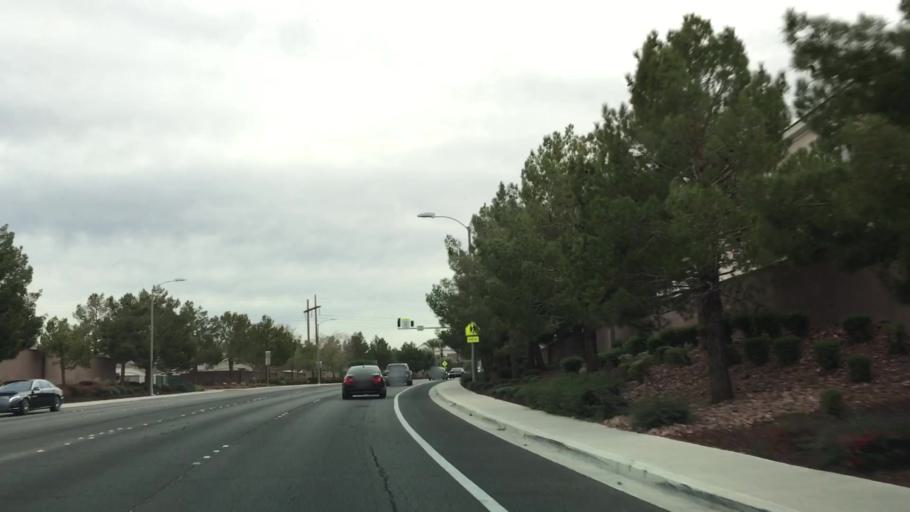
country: US
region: Nevada
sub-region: Clark County
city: Whitney
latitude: 36.0173
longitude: -115.0916
